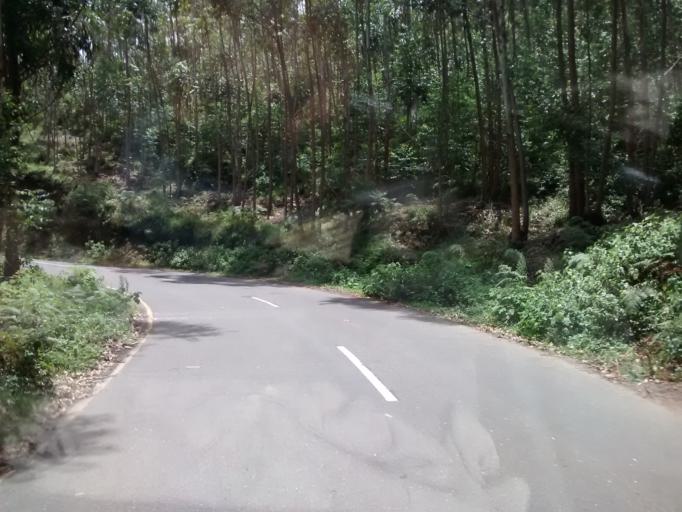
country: IN
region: Kerala
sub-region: Idukki
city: Munnar
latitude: 10.1314
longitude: 77.1708
